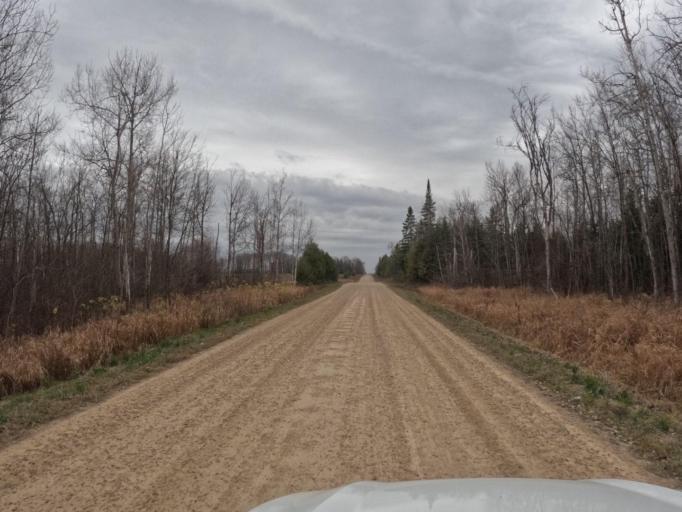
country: CA
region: Ontario
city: Shelburne
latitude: 44.0281
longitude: -80.3936
